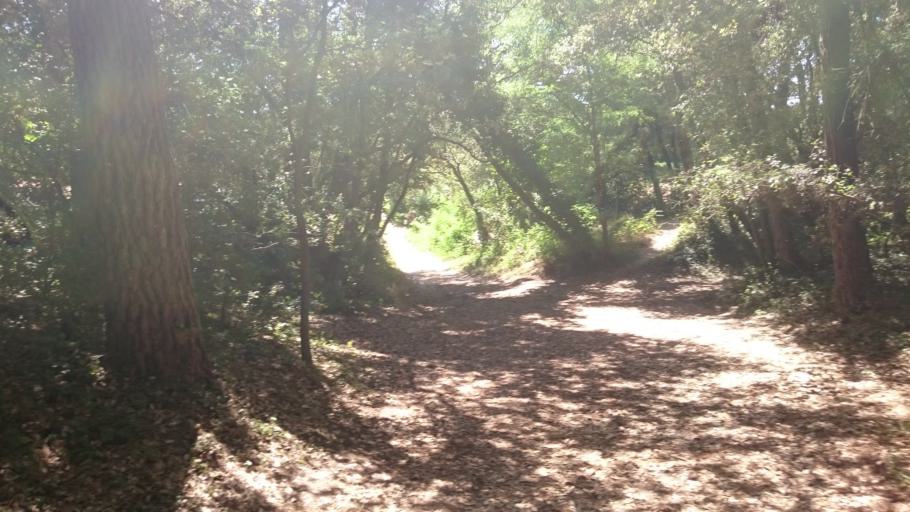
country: FR
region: Pays de la Loire
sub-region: Departement de la Vendee
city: Longeville-sur-Mer
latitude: 46.4061
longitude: -1.5120
